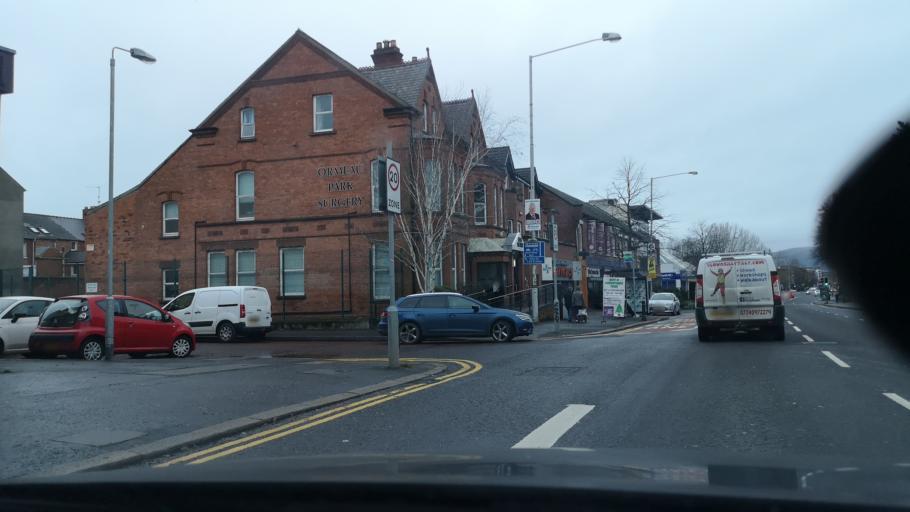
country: GB
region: Northern Ireland
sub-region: City of Belfast
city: Belfast
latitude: 54.5805
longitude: -5.9208
